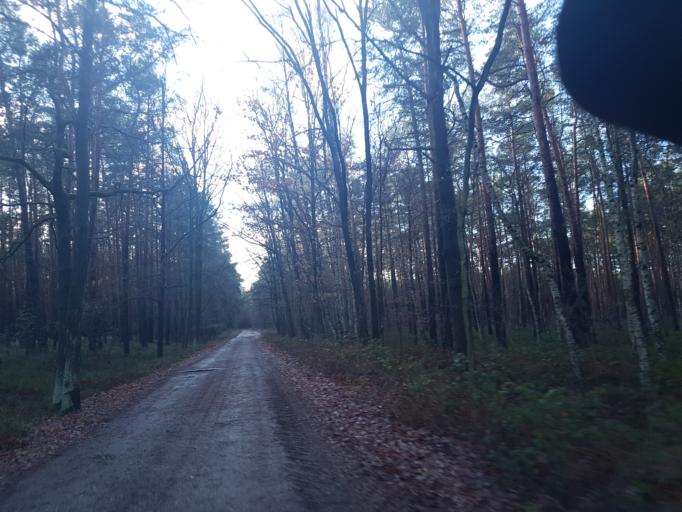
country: DE
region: Brandenburg
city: Ruckersdorf
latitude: 51.5899
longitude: 13.6024
